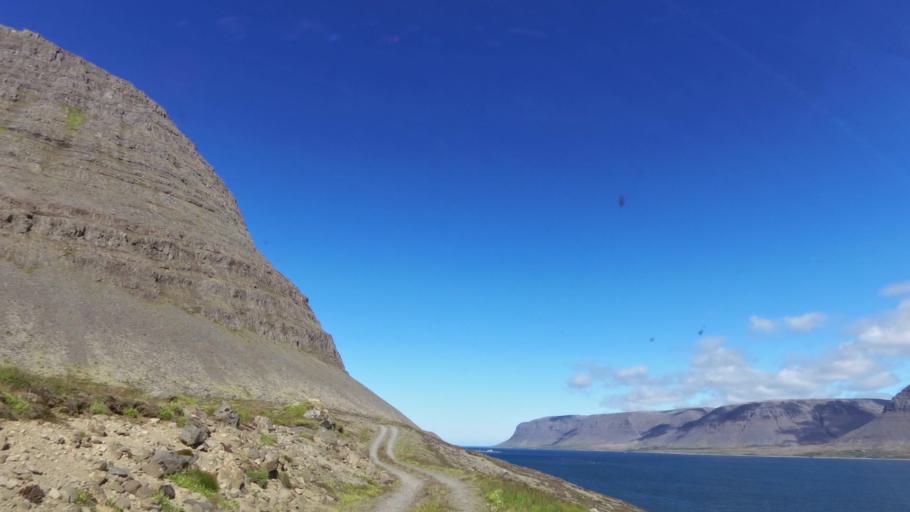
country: IS
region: West
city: Olafsvik
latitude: 65.6253
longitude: -23.8964
